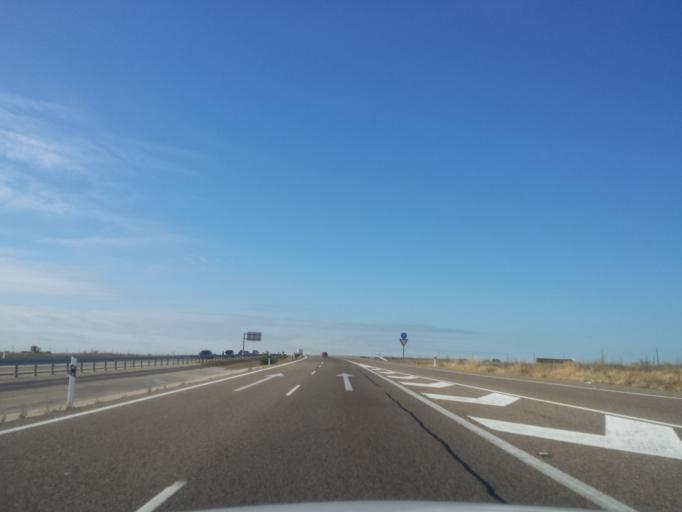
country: ES
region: Castille and Leon
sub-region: Provincia de Leon
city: Ardon
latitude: 42.4364
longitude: -5.5855
